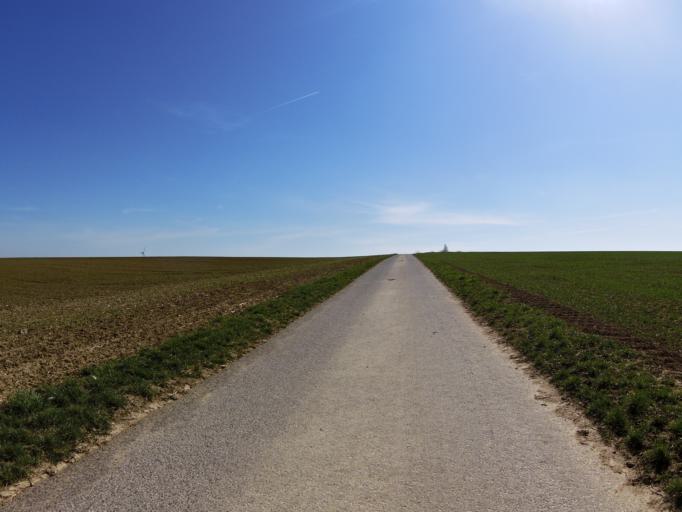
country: DE
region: Bavaria
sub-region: Regierungsbezirk Unterfranken
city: Prosselsheim
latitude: 49.8543
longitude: 10.1311
